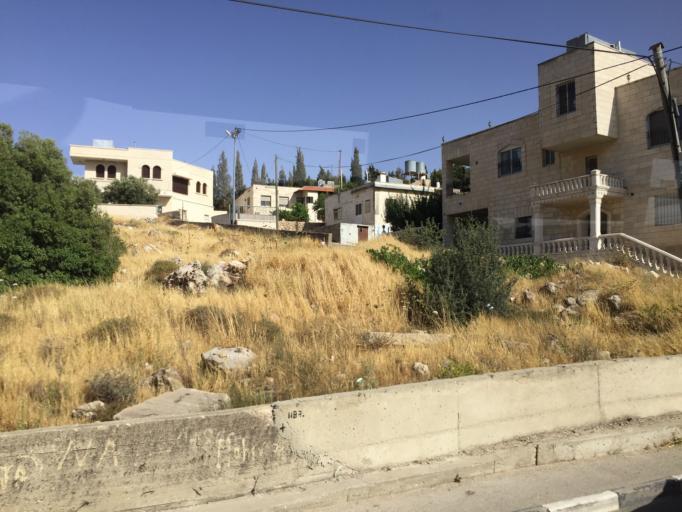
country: PS
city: Ad Dawhah
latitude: 31.7107
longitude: 35.1739
